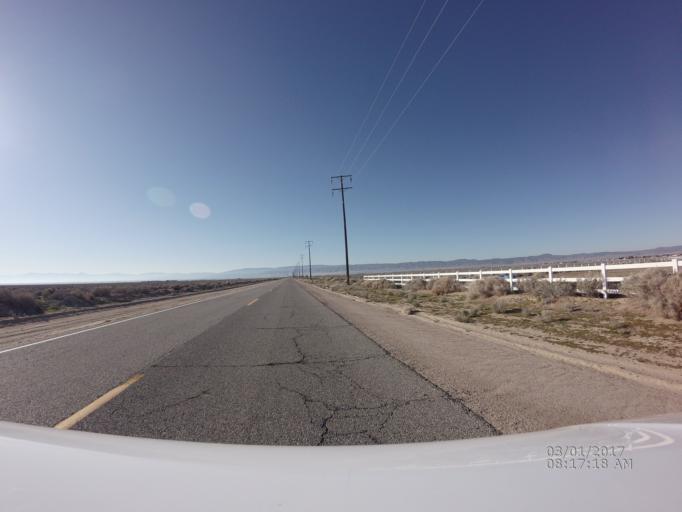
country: US
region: California
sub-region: Los Angeles County
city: Quartz Hill
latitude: 34.7568
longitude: -118.2547
